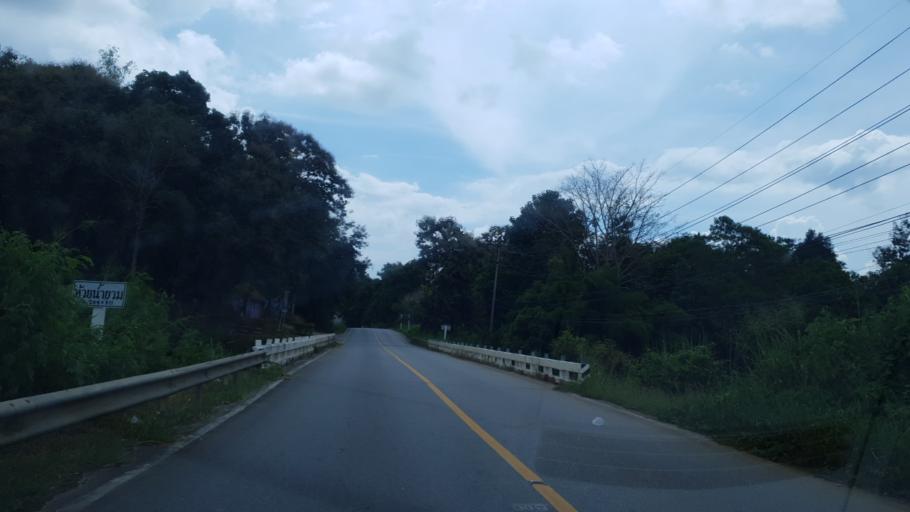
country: TH
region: Mae Hong Son
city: Khun Yuam
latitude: 18.8078
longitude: 97.9308
